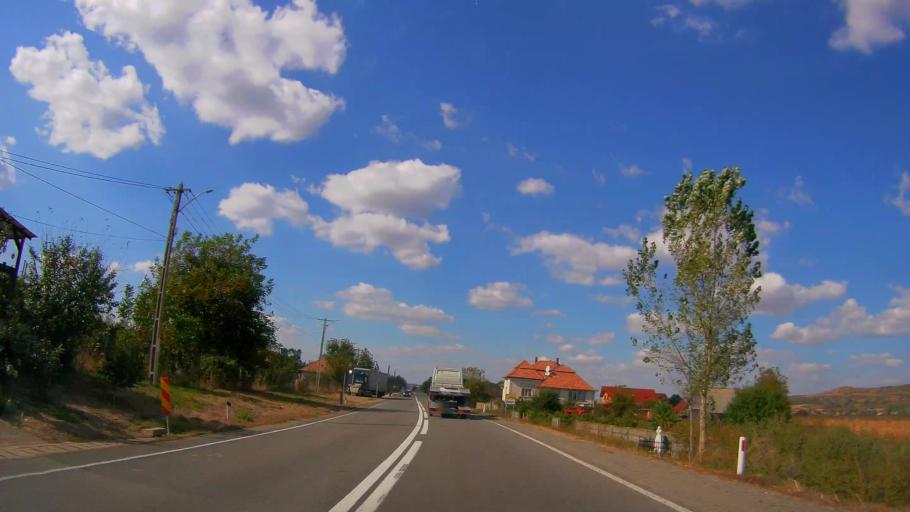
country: RO
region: Salaj
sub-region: Comuna Bobota
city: Dersida
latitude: 47.3761
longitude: 22.7869
